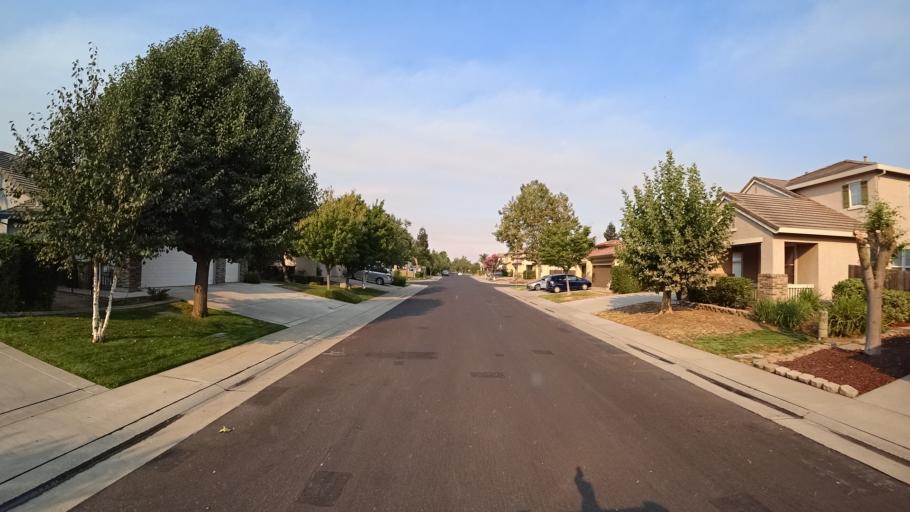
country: US
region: California
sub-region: Sacramento County
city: Laguna
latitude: 38.3865
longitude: -121.4319
